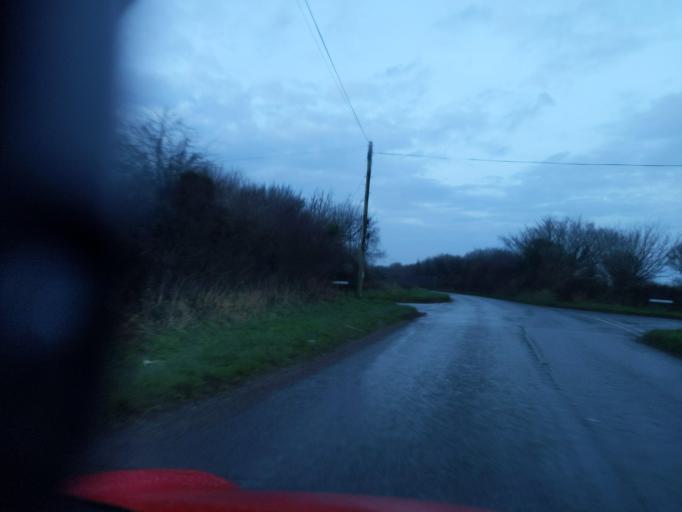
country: GB
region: England
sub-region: Devon
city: Wembury
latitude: 50.3442
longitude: -4.0760
